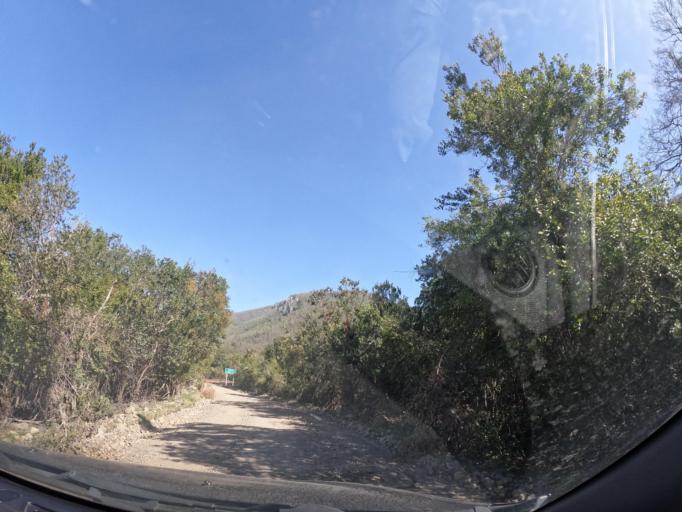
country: CL
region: Maule
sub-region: Provincia de Linares
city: Longavi
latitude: -36.2857
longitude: -71.4160
